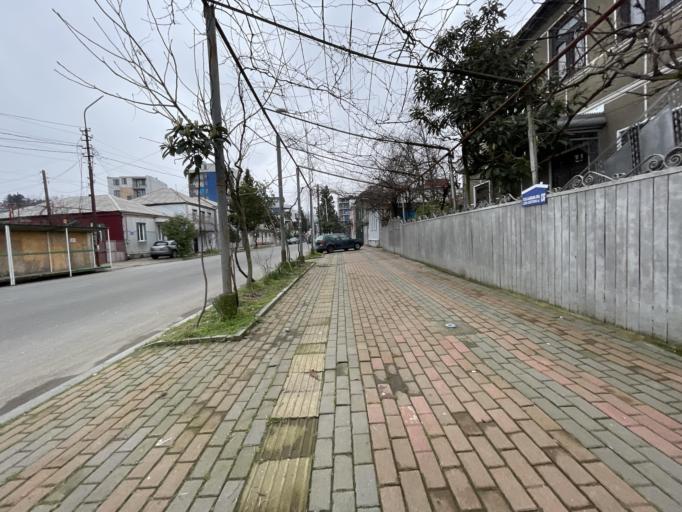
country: GE
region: Ajaria
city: Batumi
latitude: 41.6384
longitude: 41.6411
